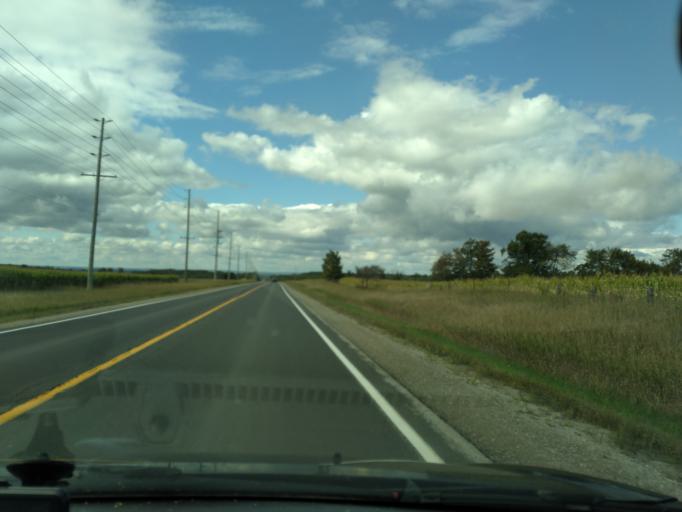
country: CA
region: Ontario
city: Innisfil
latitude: 44.2667
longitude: -79.7402
